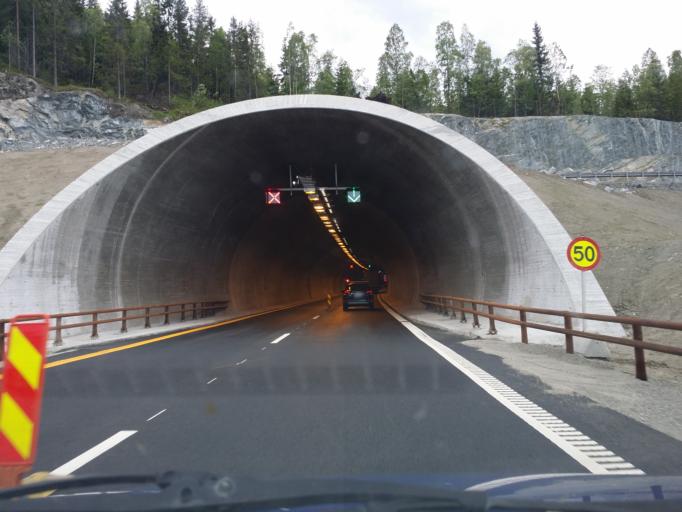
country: NO
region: Akershus
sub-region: Eidsvoll
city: Eidsvoll
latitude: 60.4392
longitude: 11.2418
